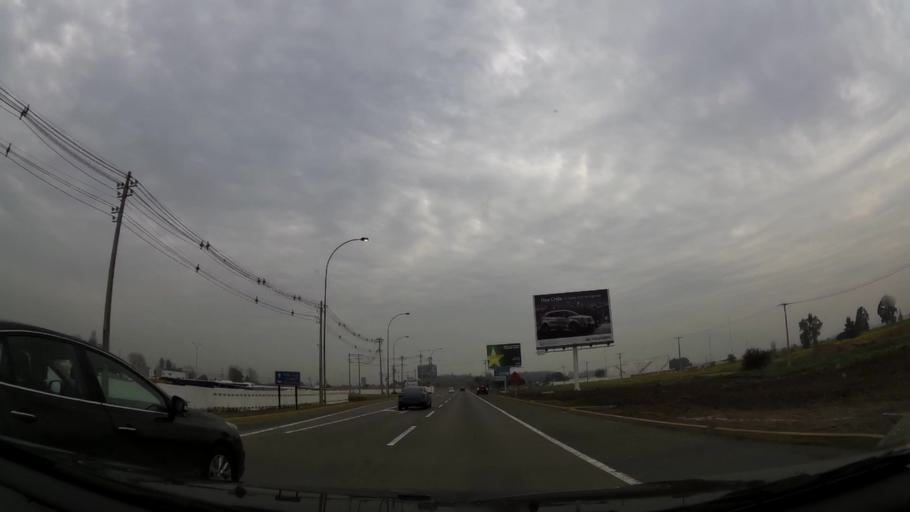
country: CL
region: Santiago Metropolitan
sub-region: Provincia de Santiago
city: Lo Prado
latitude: -33.4068
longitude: -70.7946
